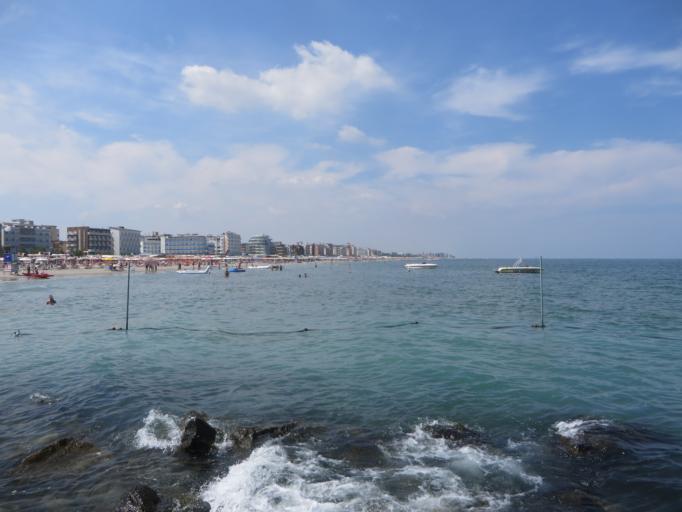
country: IT
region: Emilia-Romagna
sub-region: Provincia di Ravenna
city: Cervia
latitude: 44.2808
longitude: 12.3543
